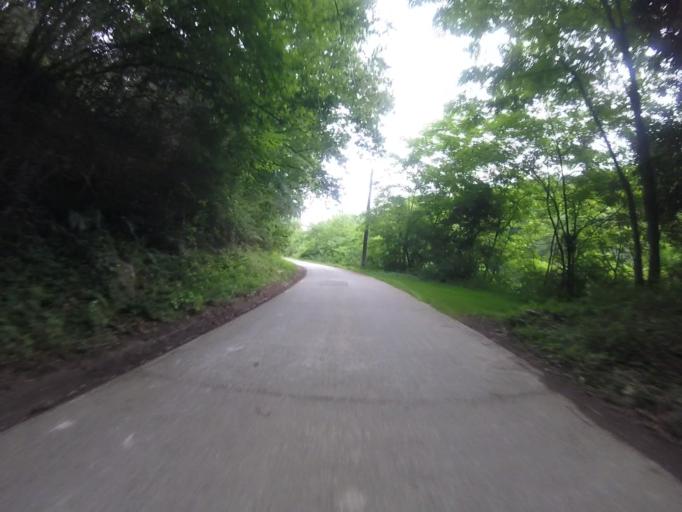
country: ES
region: Navarre
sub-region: Provincia de Navarra
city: Sunbilla
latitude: 43.1504
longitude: -1.6689
